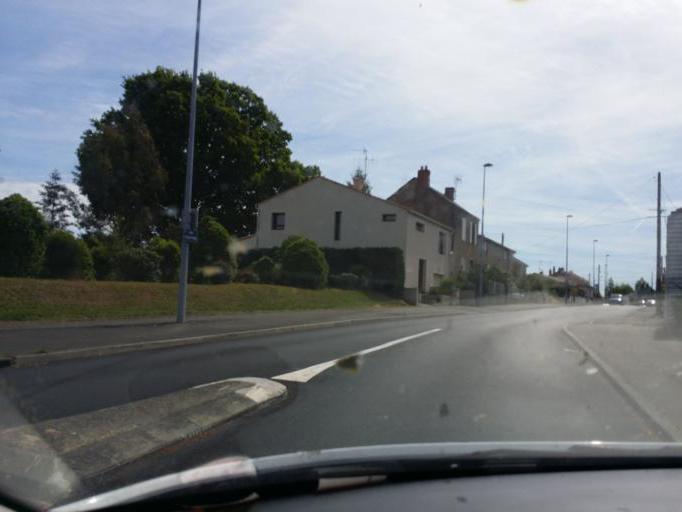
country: FR
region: Pays de la Loire
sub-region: Departement de la Vendee
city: La Roche-sur-Yon
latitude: 46.6649
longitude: -1.4147
